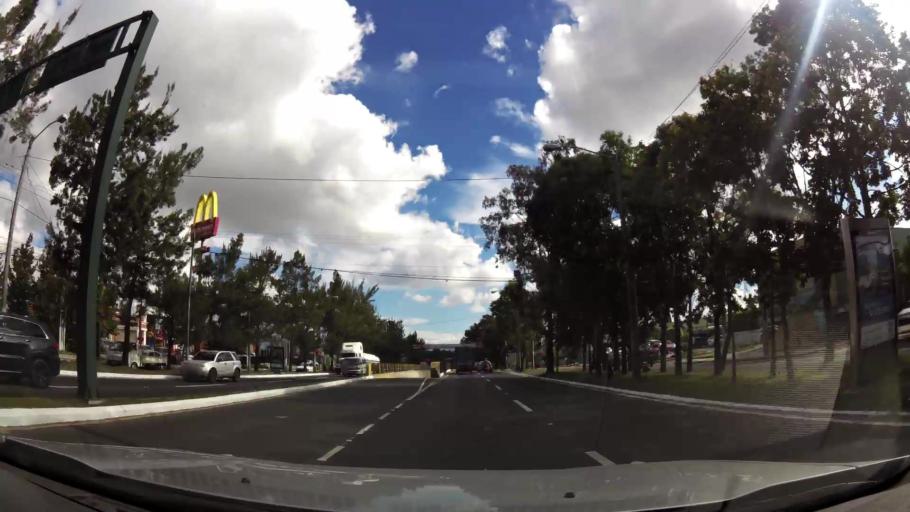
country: GT
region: Guatemala
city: Guatemala City
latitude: 14.6195
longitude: -90.5566
